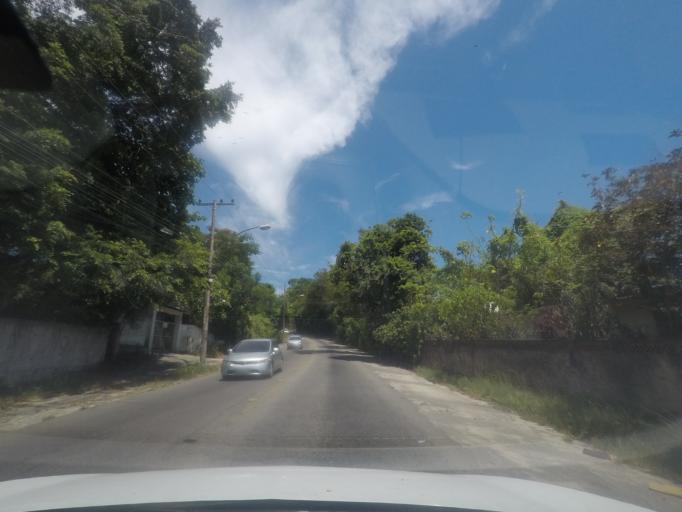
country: BR
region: Rio de Janeiro
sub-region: Itaguai
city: Itaguai
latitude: -23.0003
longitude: -43.6469
